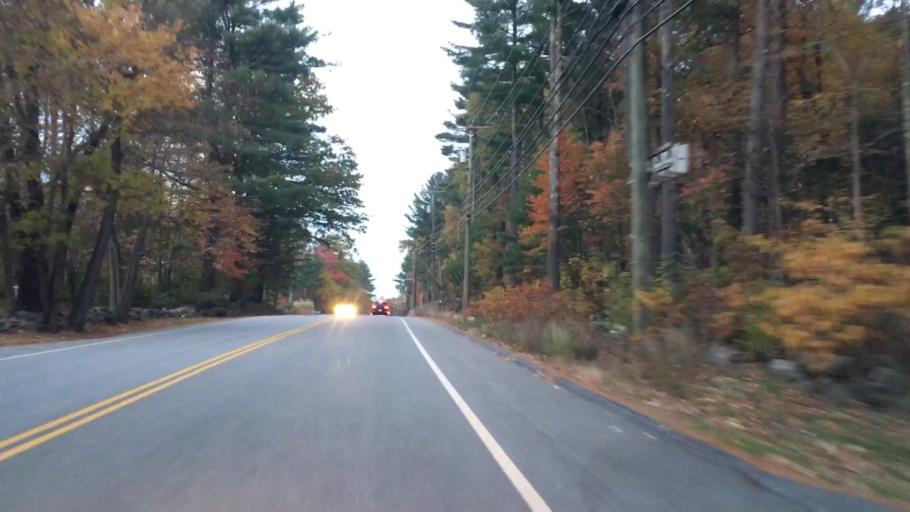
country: US
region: New Hampshire
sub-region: Hillsborough County
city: Milford
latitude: 42.8498
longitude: -71.6354
